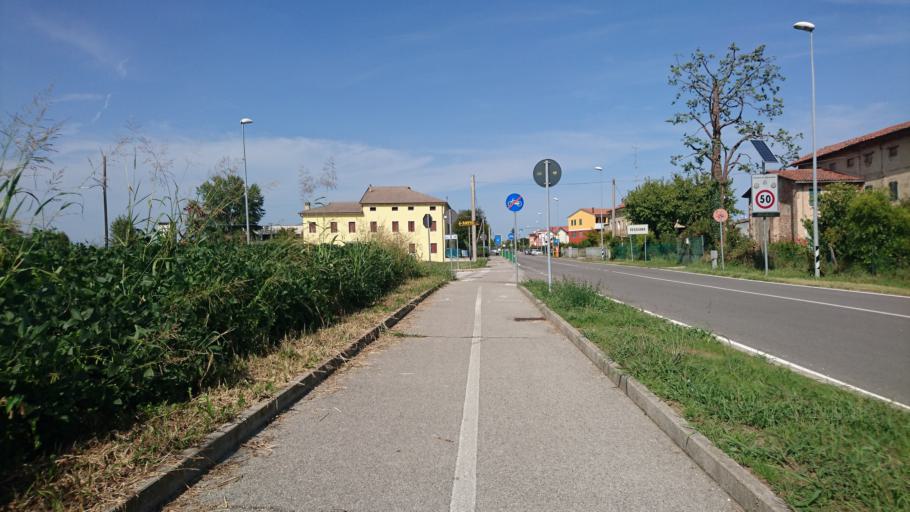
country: IT
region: Veneto
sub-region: Provincia di Padova
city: Veggiano
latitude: 45.4440
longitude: 11.7070
